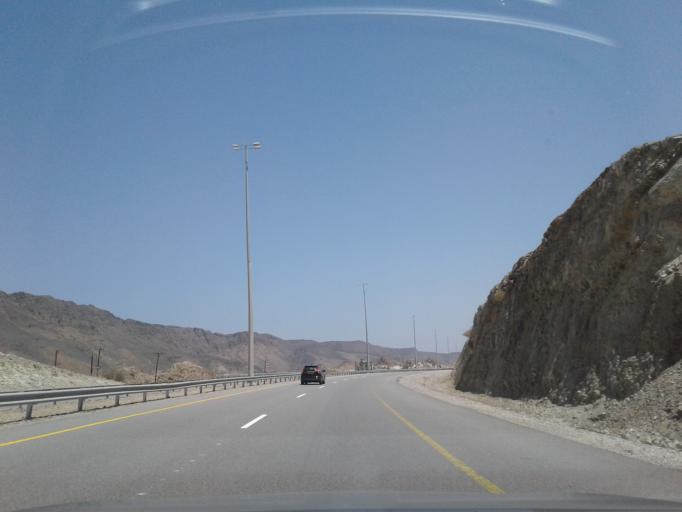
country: OM
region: Muhafazat Masqat
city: Muscat
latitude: 23.2633
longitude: 58.7642
